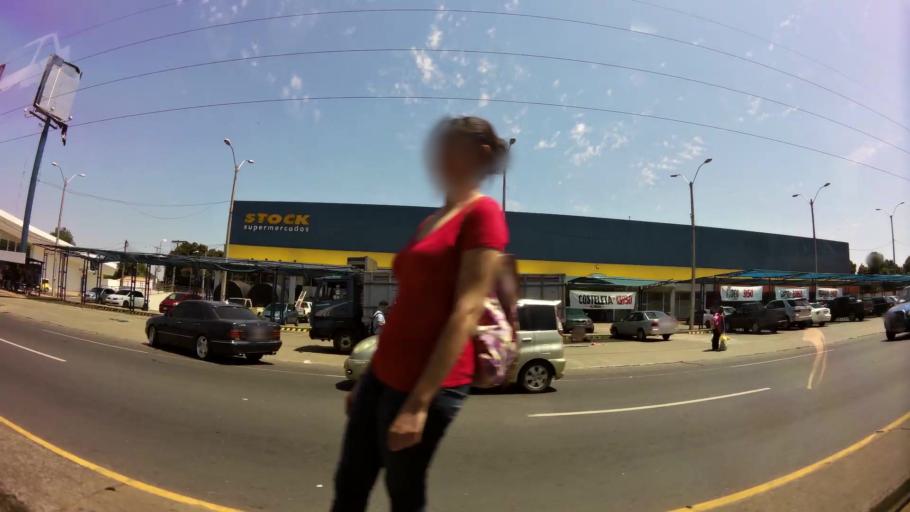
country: PY
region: Central
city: Villa Elisa
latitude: -25.3538
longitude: -57.5712
